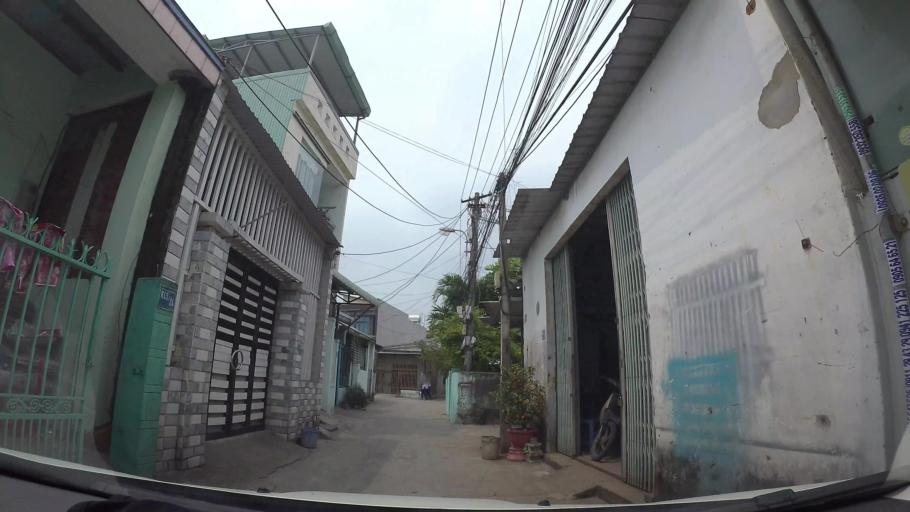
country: VN
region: Da Nang
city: Son Tra
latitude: 16.0985
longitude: 108.2498
